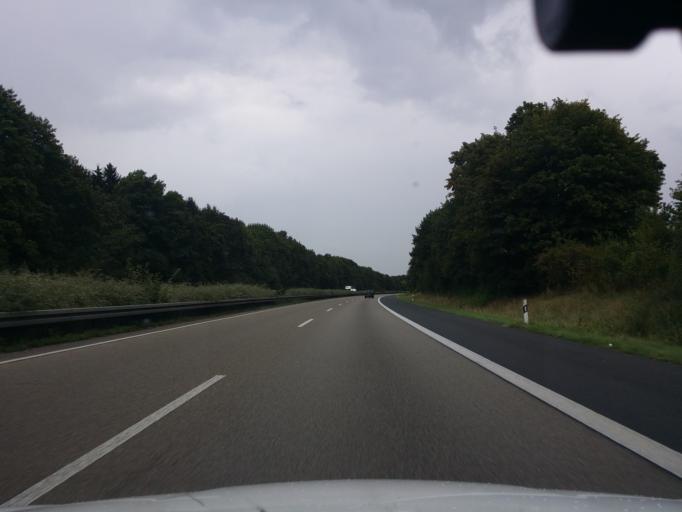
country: DE
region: Hesse
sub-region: Regierungsbezirk Kassel
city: Kunzell
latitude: 50.5368
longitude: 9.7308
